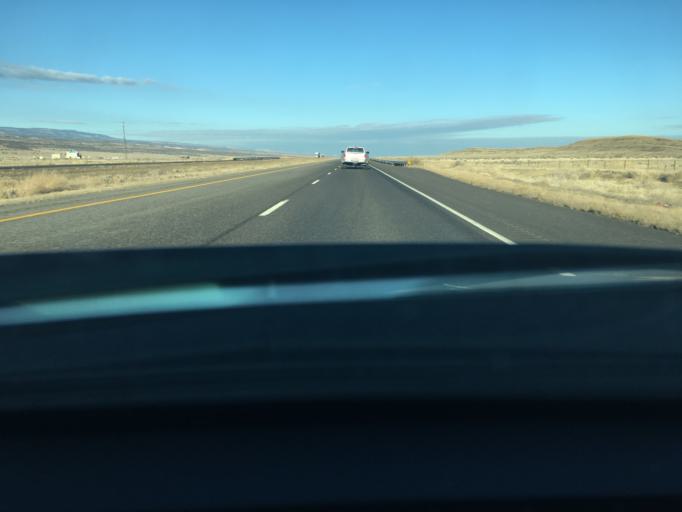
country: US
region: Colorado
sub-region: Mesa County
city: Palisade
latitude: 38.8683
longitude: -108.3322
